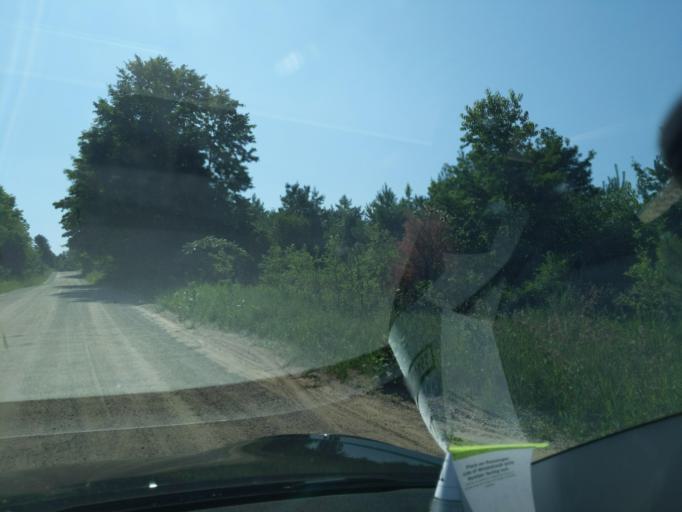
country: US
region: Michigan
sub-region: Mackinac County
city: Saint Ignace
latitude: 45.6980
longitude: -84.7217
